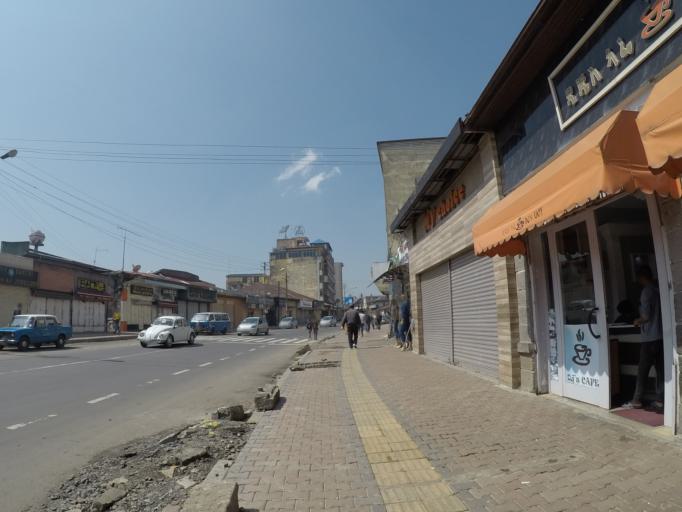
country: ET
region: Adis Abeba
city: Addis Ababa
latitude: 9.0363
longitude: 38.7545
